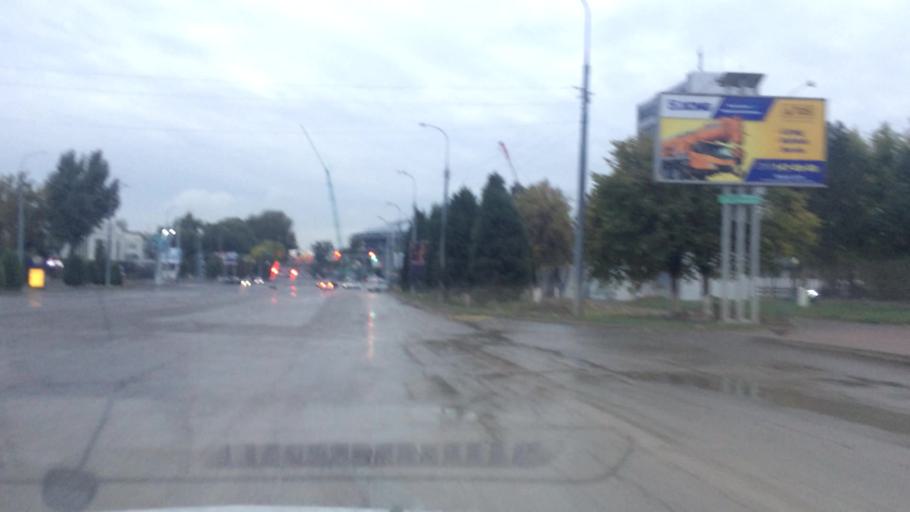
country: UZ
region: Toshkent Shahri
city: Tashkent
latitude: 41.3129
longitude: 69.2535
